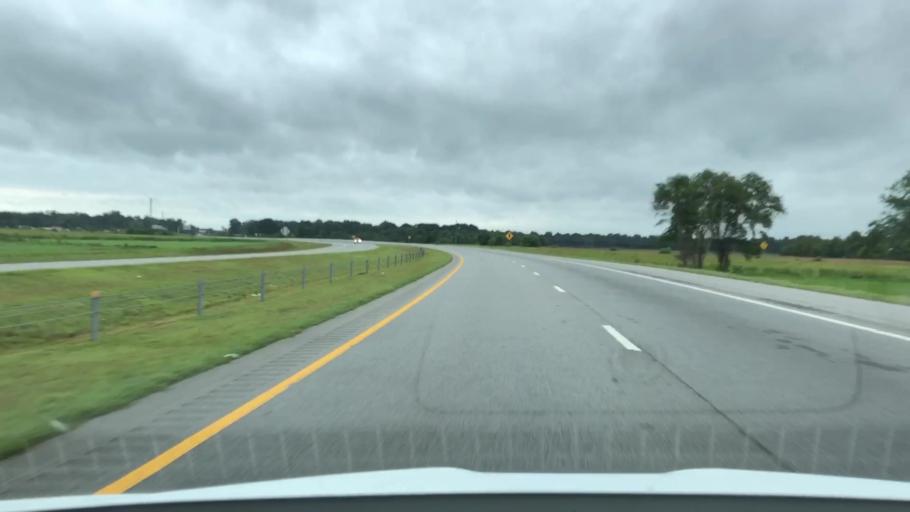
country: US
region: North Carolina
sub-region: Lenoir County
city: Kinston
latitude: 35.2658
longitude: -77.6778
